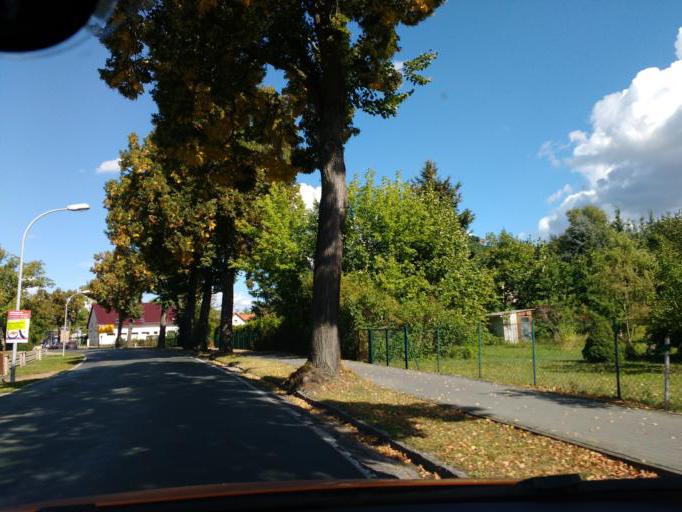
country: DE
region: Brandenburg
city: Bestensee
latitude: 52.2403
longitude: 13.6339
